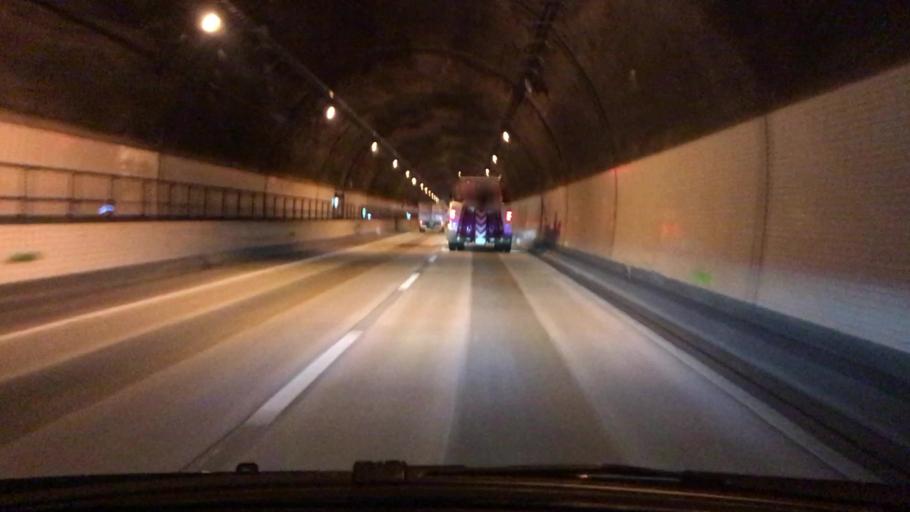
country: JP
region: Hyogo
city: Kobe
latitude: 34.7797
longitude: 135.2124
